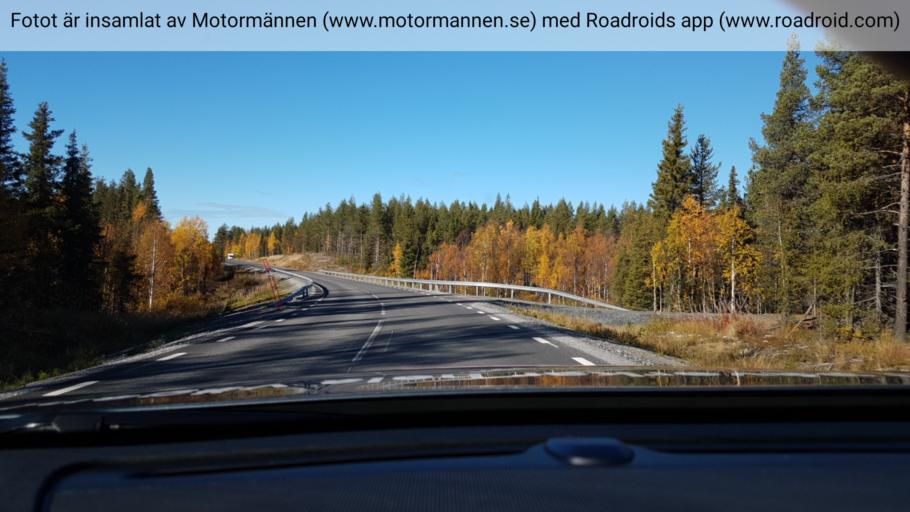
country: SE
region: Norrbotten
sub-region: Gallivare Kommun
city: Gaellivare
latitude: 66.8362
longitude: 21.0402
